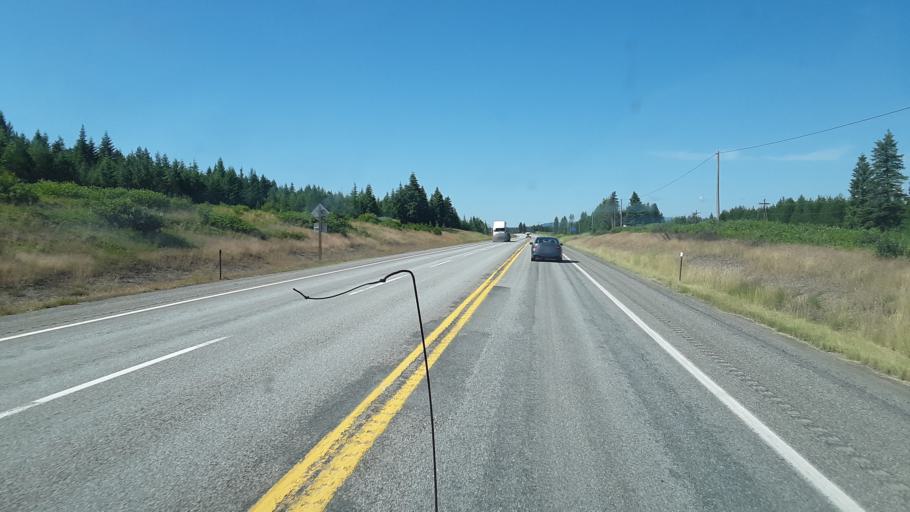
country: US
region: Idaho
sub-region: Kootenai County
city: Spirit Lake
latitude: 48.0078
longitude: -116.6675
